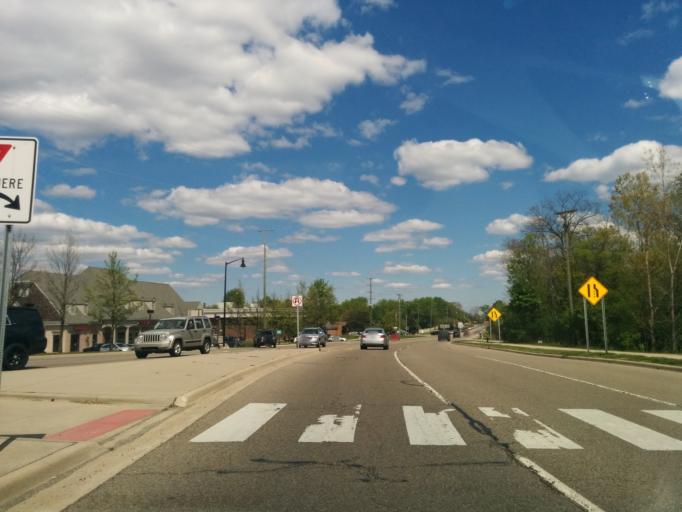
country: US
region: Michigan
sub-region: Oakland County
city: West Bloomfield Township
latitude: 42.5277
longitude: -83.3794
